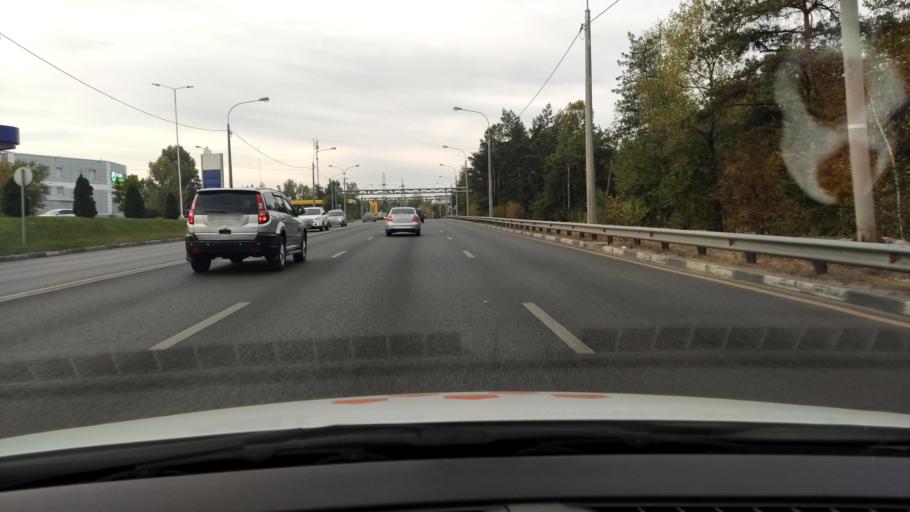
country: RU
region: Voronezj
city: Pridonskoy
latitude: 51.6825
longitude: 39.1166
